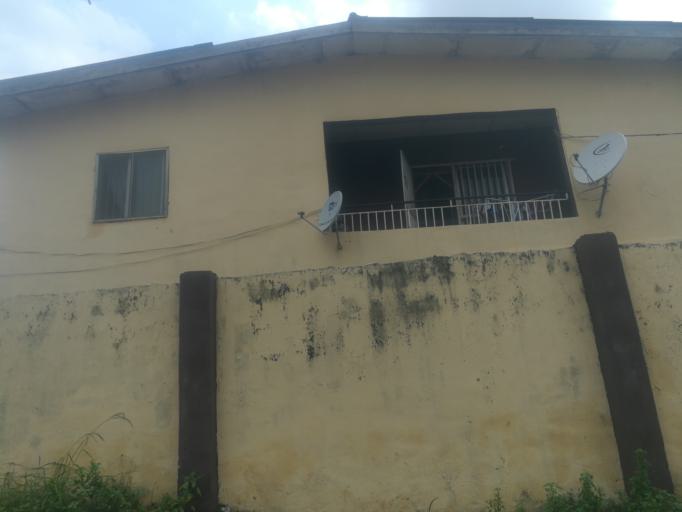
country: NG
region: Lagos
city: Ojota
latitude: 6.5604
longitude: 3.3916
